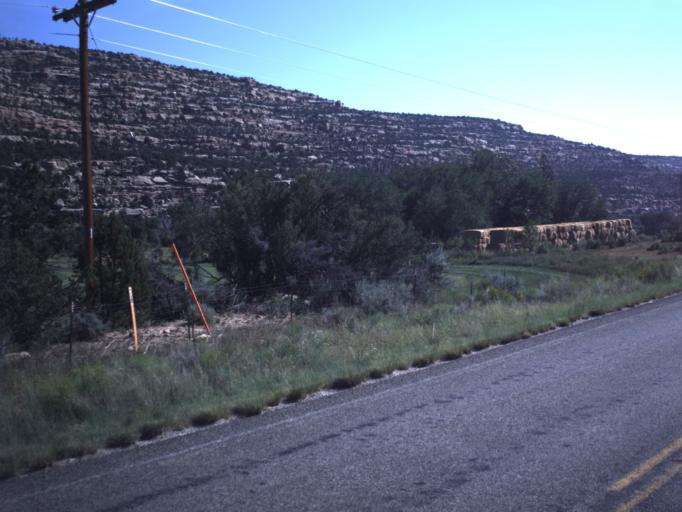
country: US
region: Utah
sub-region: Duchesne County
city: Duchesne
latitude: 40.2963
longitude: -110.5757
